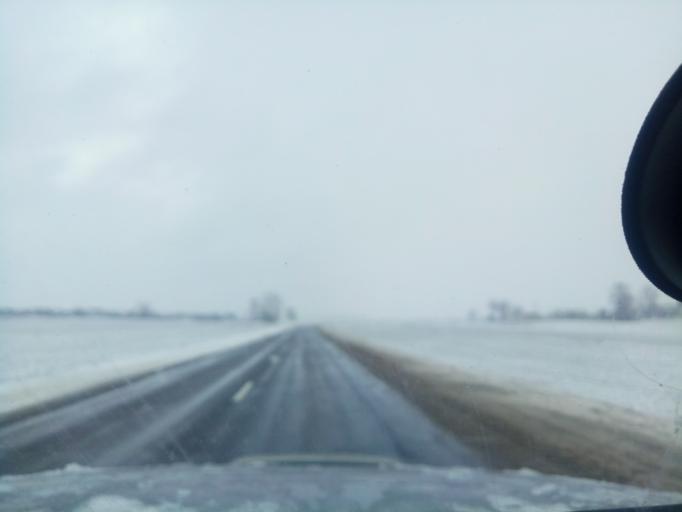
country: BY
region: Minsk
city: Haradzyeya
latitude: 53.3039
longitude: 26.5733
